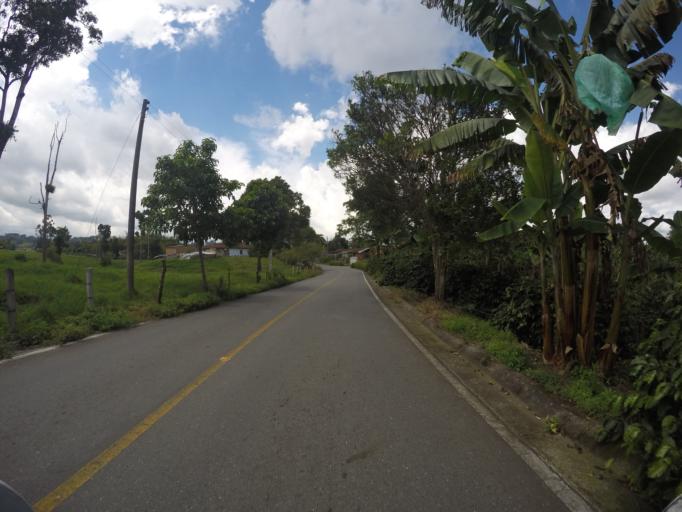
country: CO
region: Quindio
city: Quimbaya
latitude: 4.6355
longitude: -75.7041
